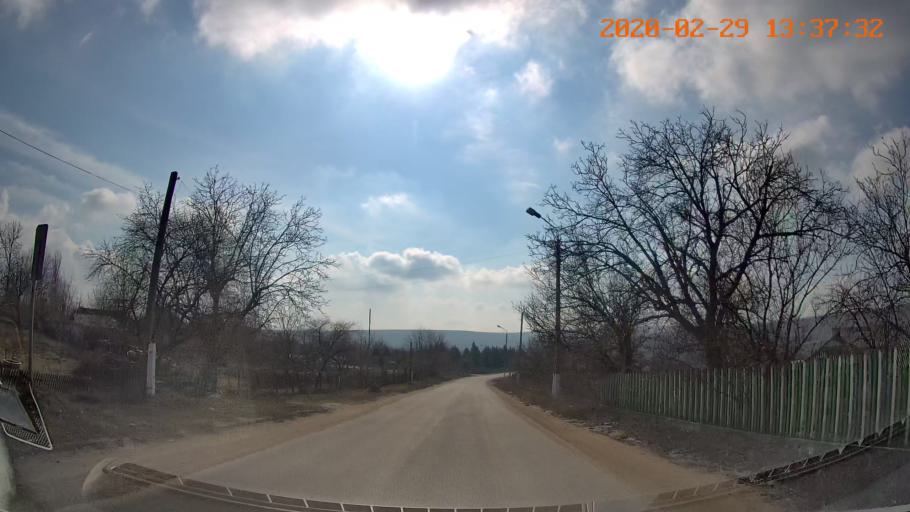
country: MD
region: Telenesti
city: Camenca
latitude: 47.8621
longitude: 28.6019
